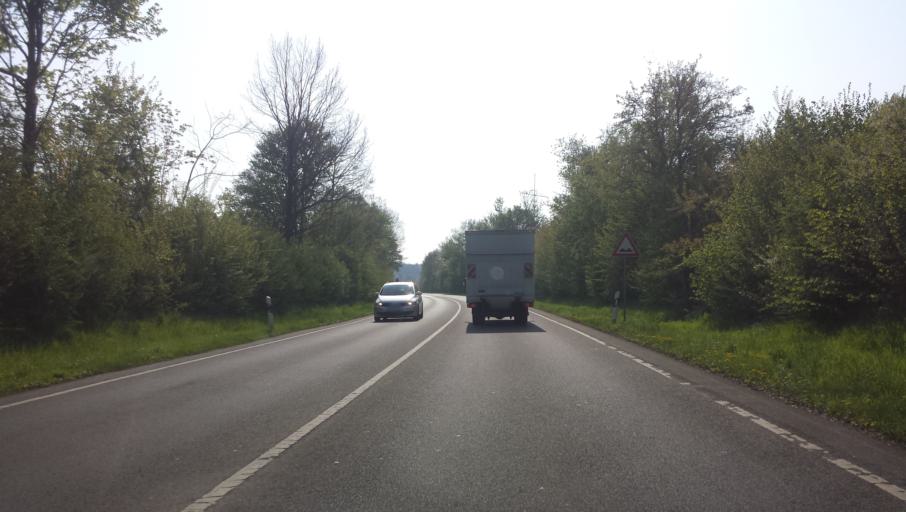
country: DE
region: Baden-Wuerttemberg
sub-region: Karlsruhe Region
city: Nussloch
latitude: 49.3102
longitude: 8.6879
